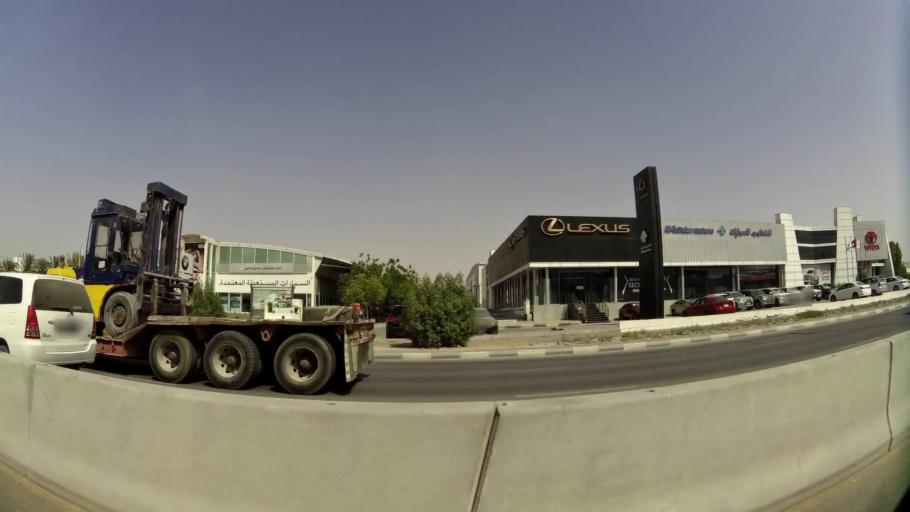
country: AE
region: Ash Shariqah
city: Sharjah
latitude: 25.3183
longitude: 55.4276
